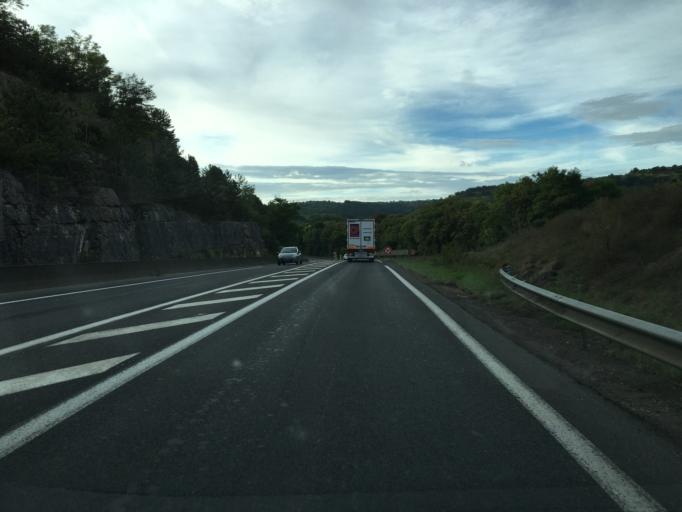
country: FR
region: Bourgogne
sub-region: Departement de la Cote-d'Or
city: Plombieres-les-Dijon
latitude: 47.3328
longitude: 4.9776
